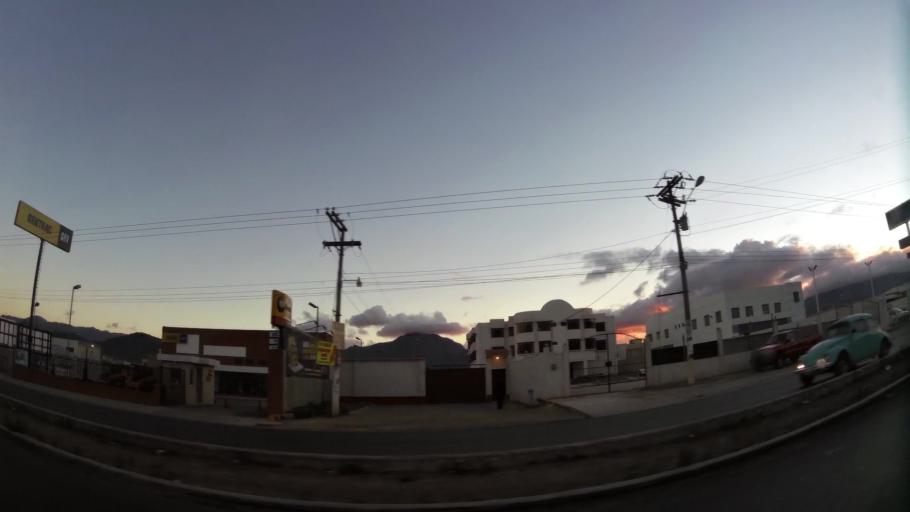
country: GT
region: Quetzaltenango
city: Quetzaltenango
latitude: 14.8587
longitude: -91.5146
